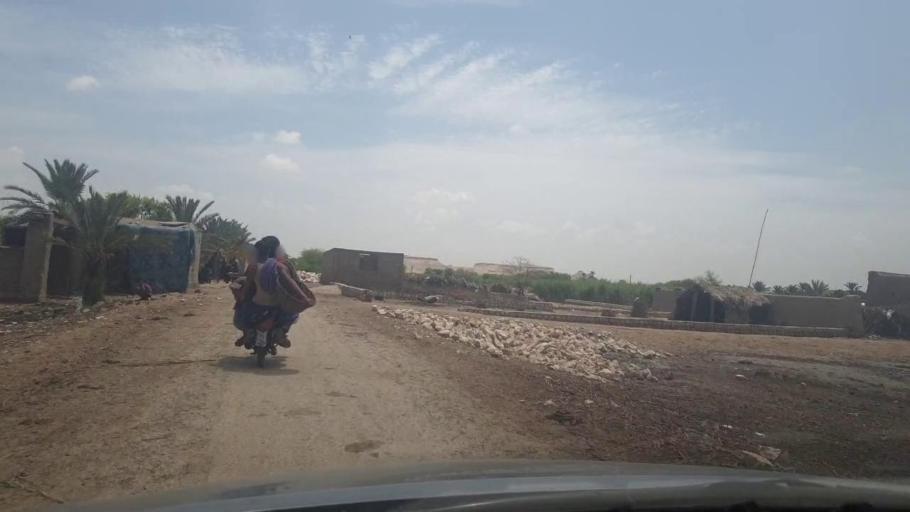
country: PK
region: Sindh
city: Kot Diji
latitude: 27.3915
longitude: 68.7636
